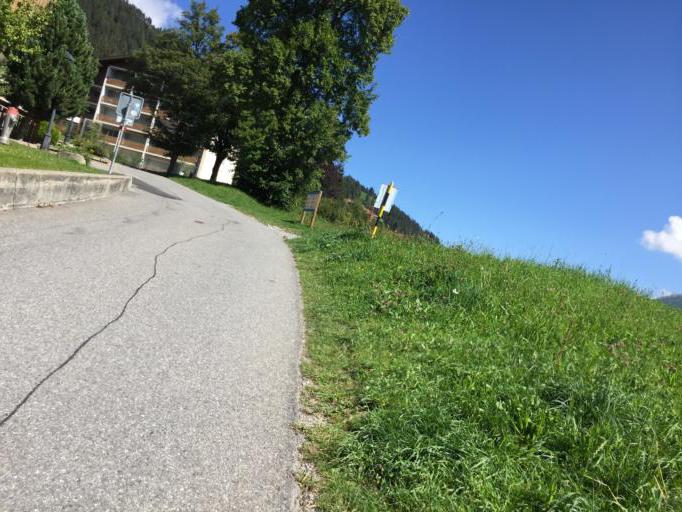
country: CH
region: Bern
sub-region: Frutigen-Niedersimmental District
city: Adelboden
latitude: 46.4888
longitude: 7.5561
